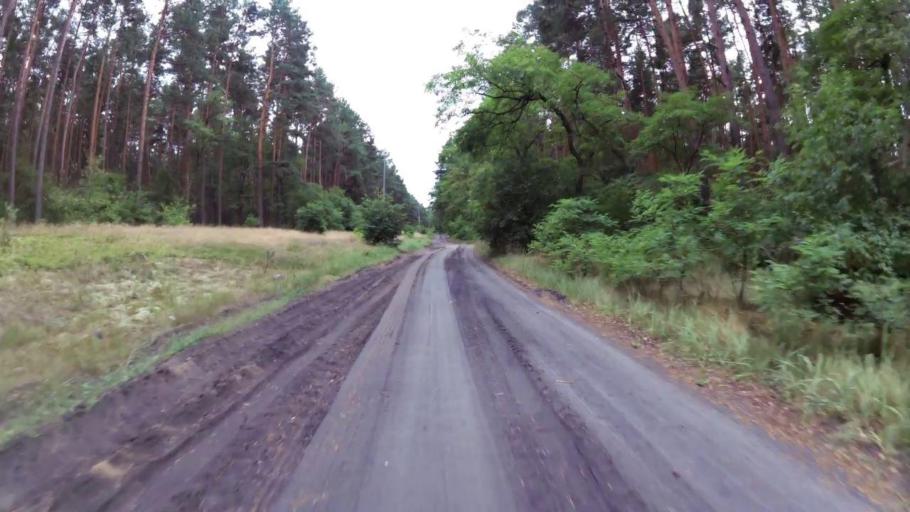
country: PL
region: West Pomeranian Voivodeship
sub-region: Powiat mysliborski
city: Debno
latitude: 52.8043
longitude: 14.7197
